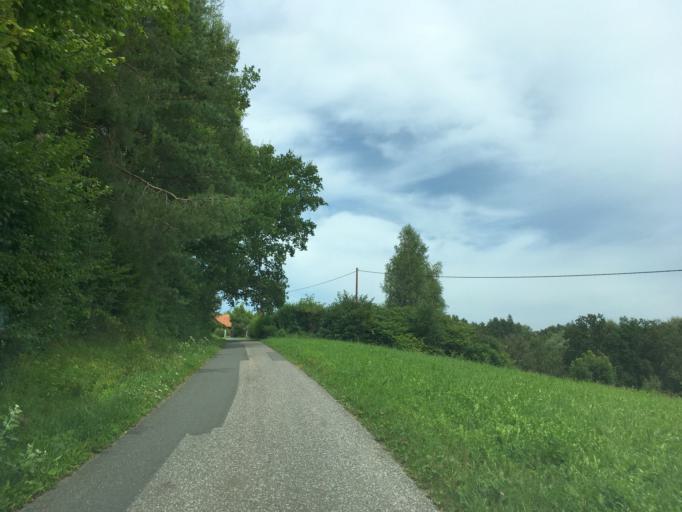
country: AT
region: Styria
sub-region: Politischer Bezirk Deutschlandsberg
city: Wettmannstatten
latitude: 46.7950
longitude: 15.4006
